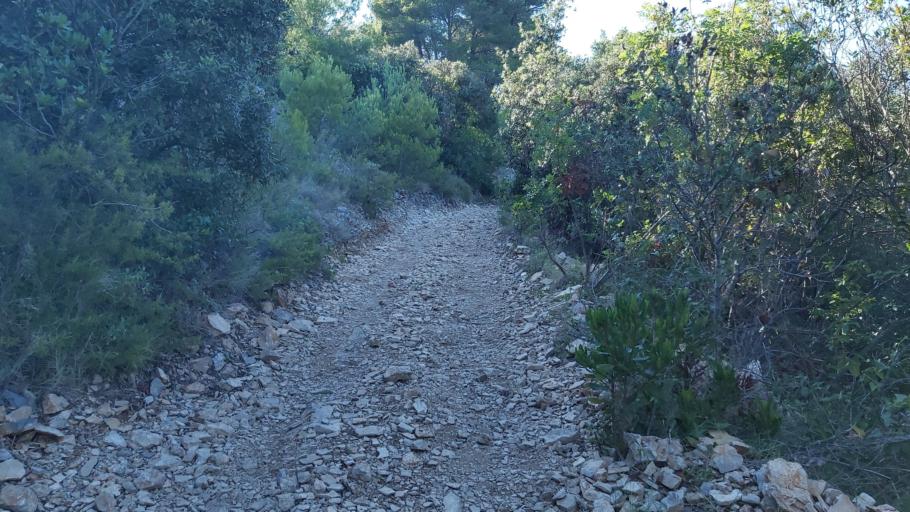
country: HR
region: Splitsko-Dalmatinska
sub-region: Grad Trogir
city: Trogir
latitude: 43.3730
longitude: 16.2873
